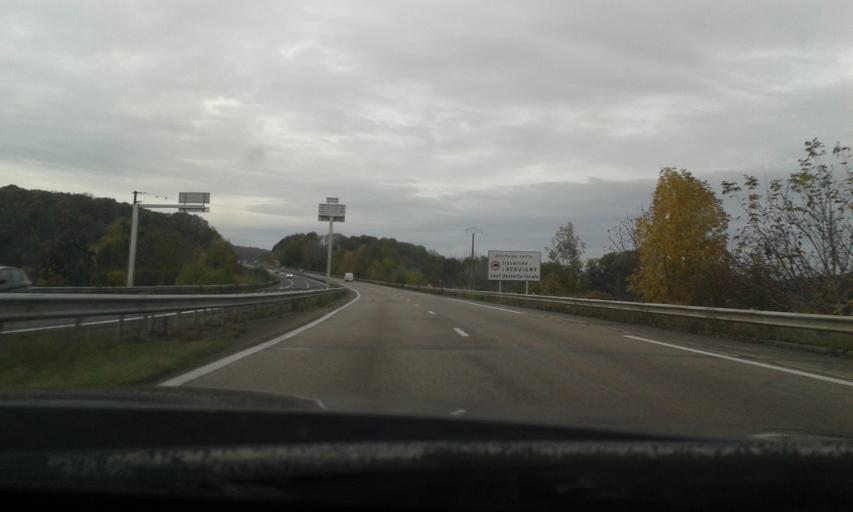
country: FR
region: Haute-Normandie
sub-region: Departement de l'Eure
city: Acquigny
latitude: 49.1589
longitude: 1.1810
